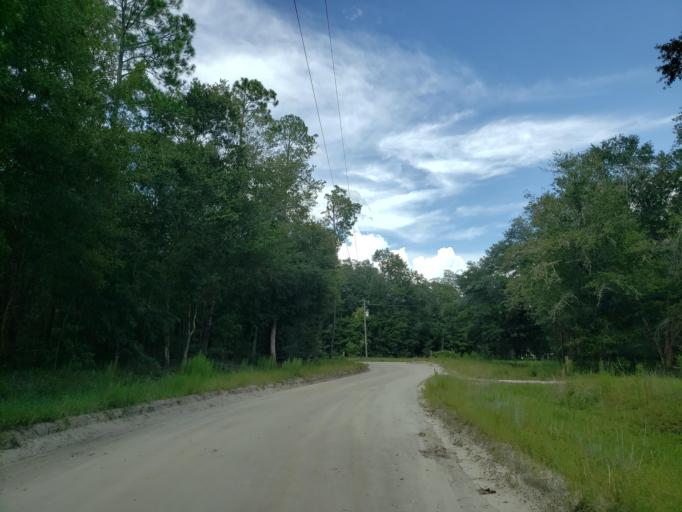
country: US
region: Florida
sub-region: Hamilton County
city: Jasper
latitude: 30.5546
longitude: -83.0892
